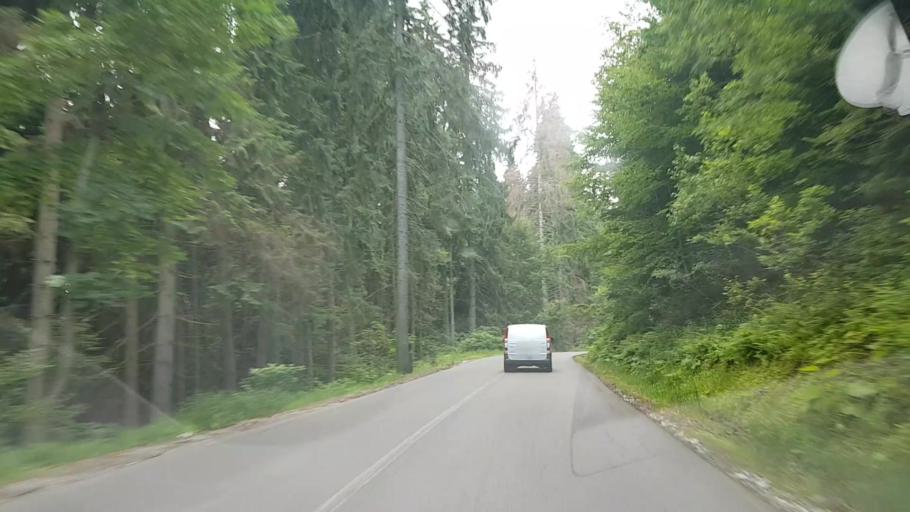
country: RO
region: Harghita
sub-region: Comuna Varsag
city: Varsag
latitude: 46.6715
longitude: 25.3251
